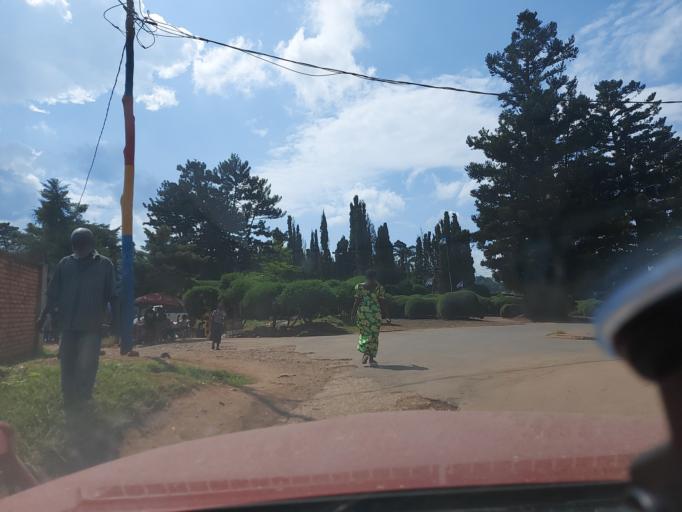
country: CD
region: South Kivu
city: Bukavu
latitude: -2.4982
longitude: 28.8681
